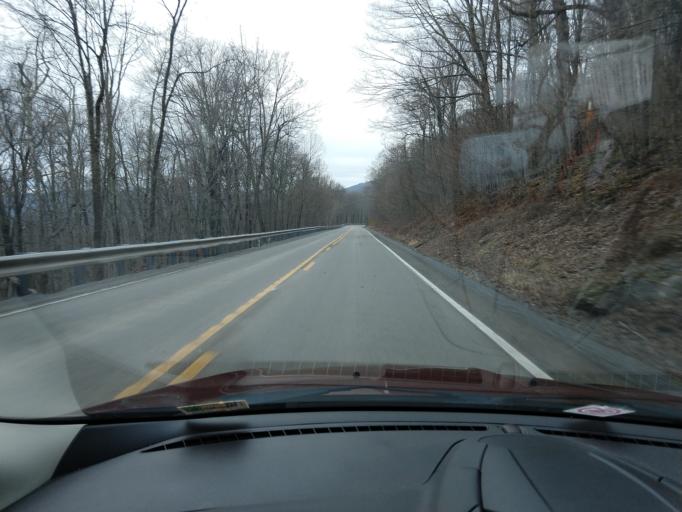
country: US
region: West Virginia
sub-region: Randolph County
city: Elkins
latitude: 38.6376
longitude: -79.9272
